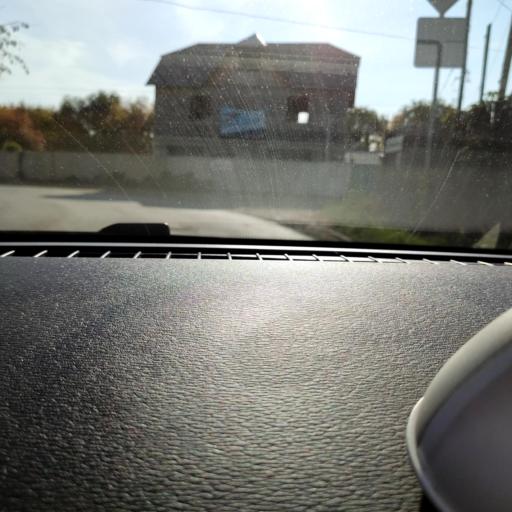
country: RU
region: Samara
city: Smyshlyayevka
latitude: 53.2361
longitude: 50.3236
